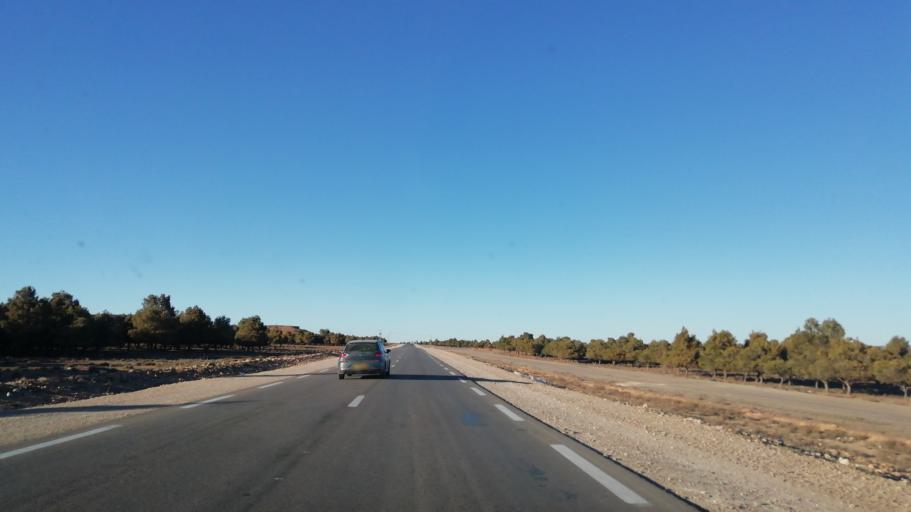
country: DZ
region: Tlemcen
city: Sebdou
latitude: 34.4959
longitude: -1.2757
